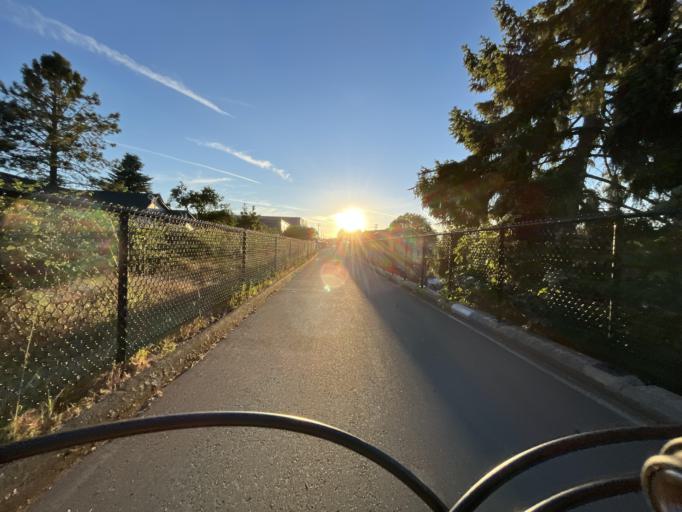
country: CA
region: British Columbia
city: Victoria
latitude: 48.4338
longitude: -123.3927
